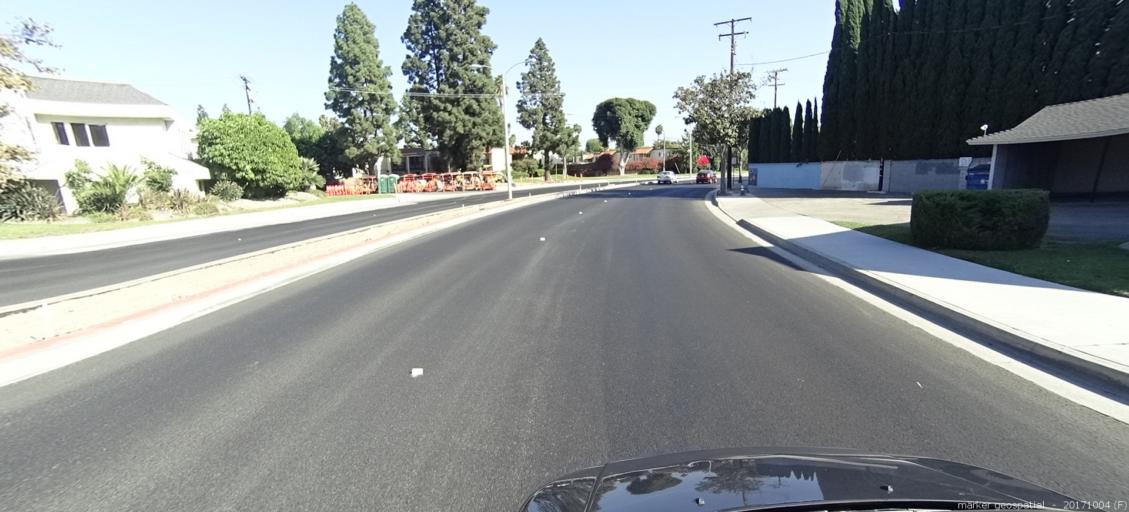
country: US
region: California
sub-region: Orange County
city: Midway City
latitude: 33.7724
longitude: -117.9734
